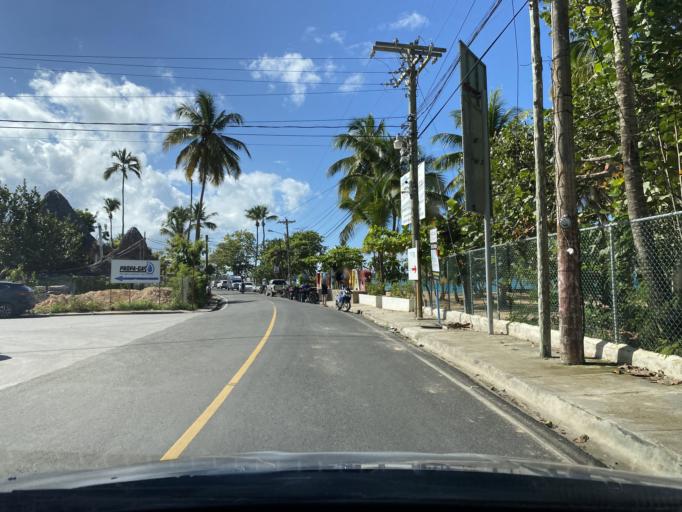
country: DO
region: Samana
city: Las Terrenas
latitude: 19.3251
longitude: -69.5292
